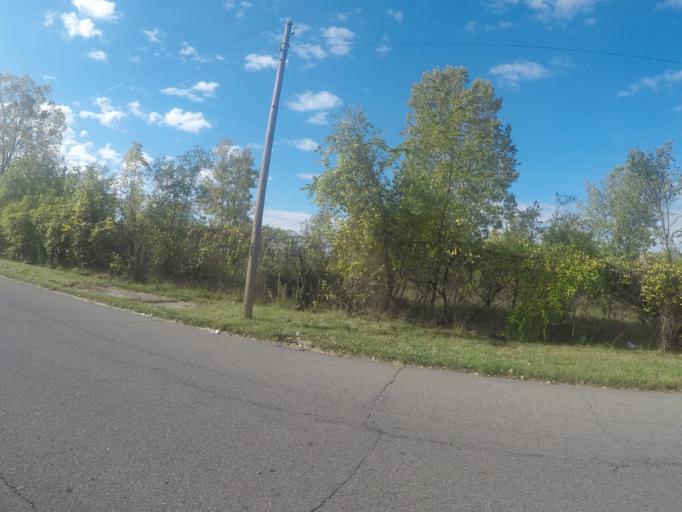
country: US
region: Michigan
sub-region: Wayne County
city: Dearborn
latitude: 42.3553
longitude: -83.1321
